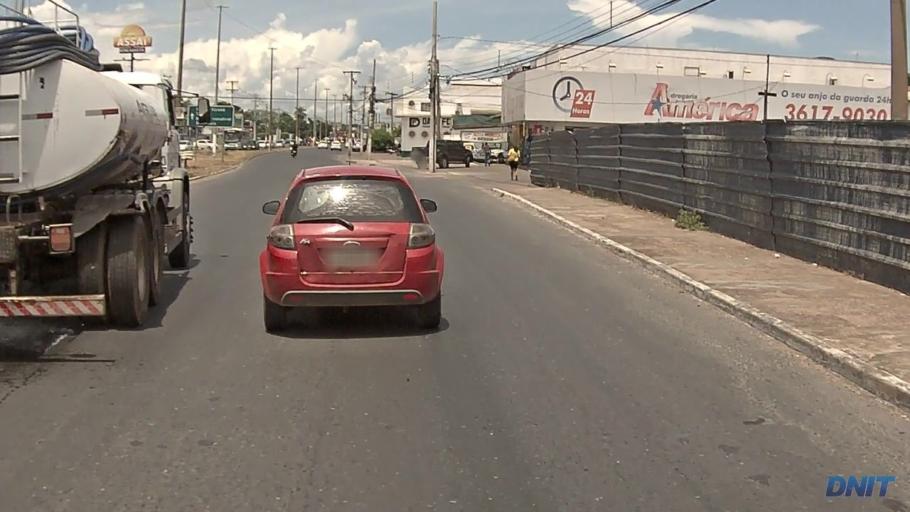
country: BR
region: Mato Grosso
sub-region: Cuiaba
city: Cuiaba
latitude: -15.6294
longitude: -56.0546
